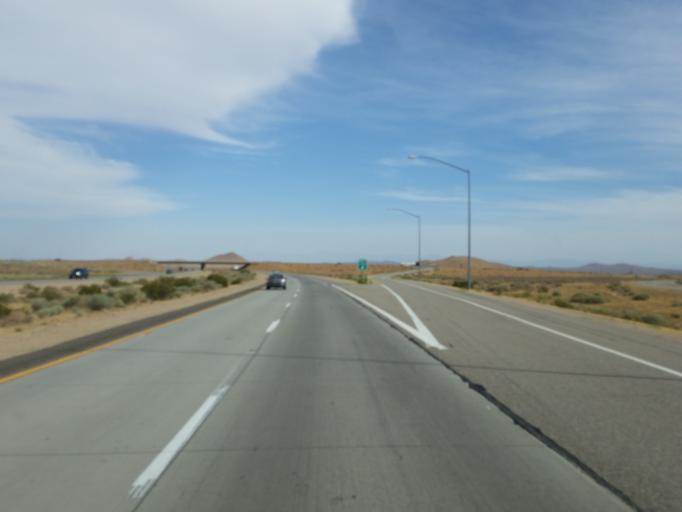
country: US
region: California
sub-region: Kern County
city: Mojave
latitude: 35.0431
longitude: -118.1111
